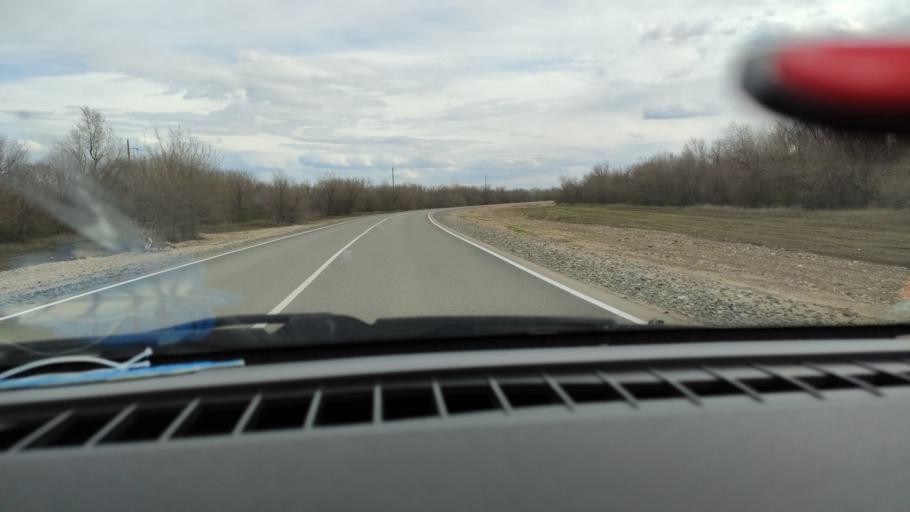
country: RU
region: Saratov
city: Privolzhskiy
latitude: 51.1528
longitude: 45.9628
